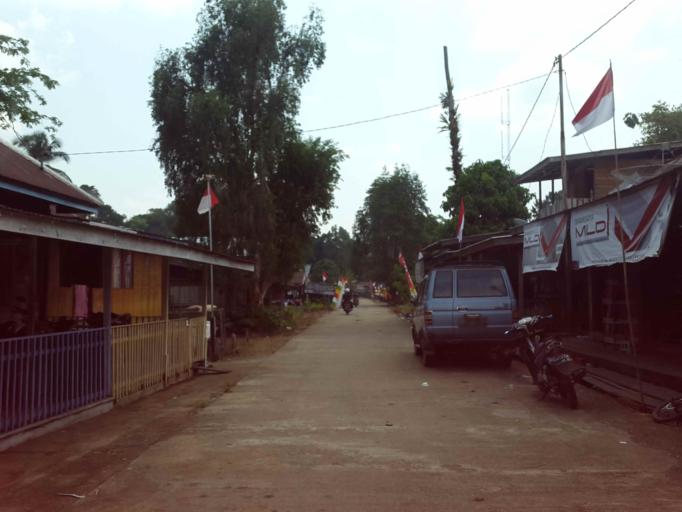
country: MY
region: Sarawak
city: Simanggang
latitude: 1.0345
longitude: 112.2296
